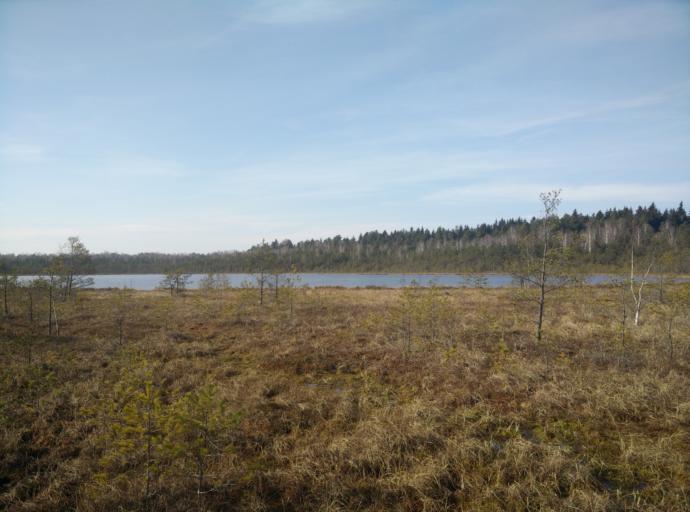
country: LT
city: Trakai
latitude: 54.6405
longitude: 24.9796
